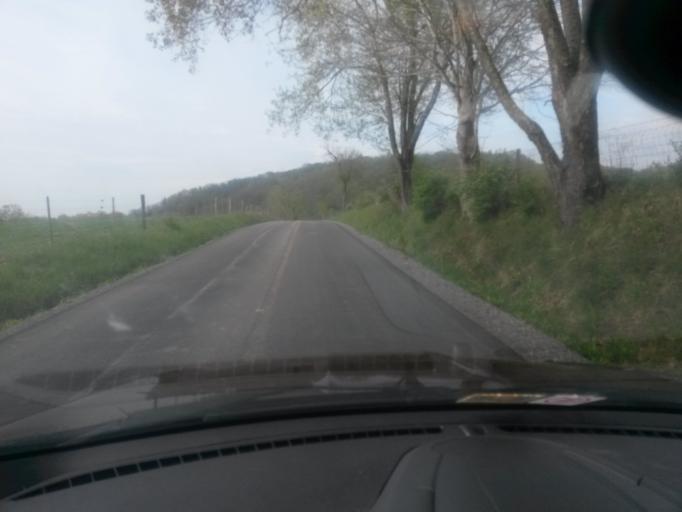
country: US
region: West Virginia
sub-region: Pocahontas County
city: Marlinton
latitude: 38.1069
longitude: -80.2240
